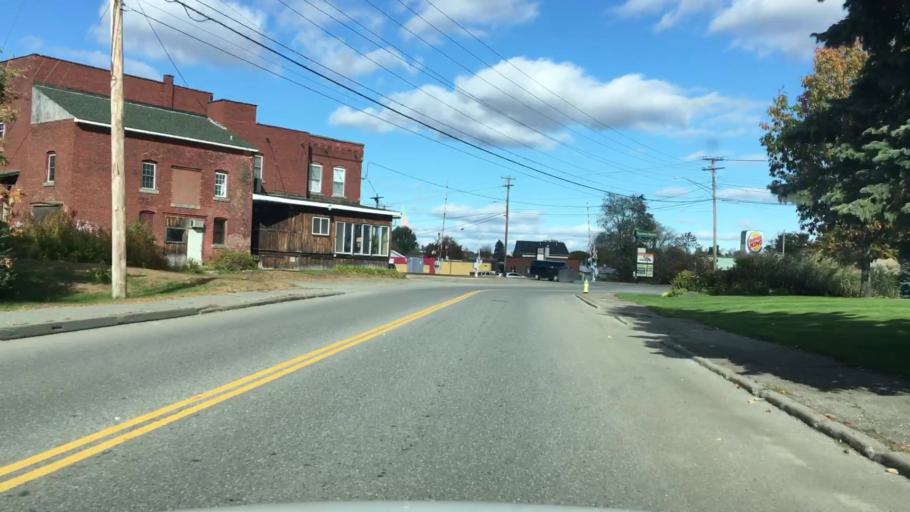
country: US
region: Maine
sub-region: Kennebec County
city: Waterville
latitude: 44.5559
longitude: -69.6327
